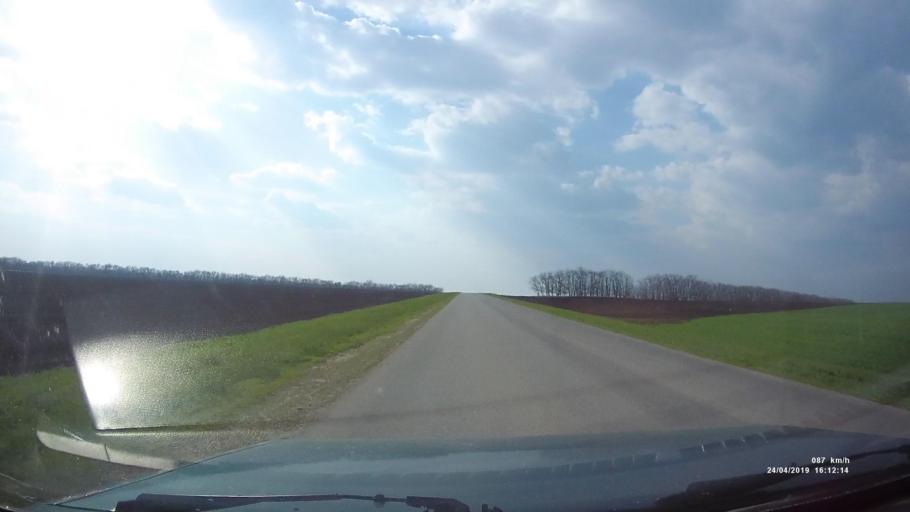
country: RU
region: Rostov
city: Sovetskoye
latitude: 46.7320
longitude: 42.2391
